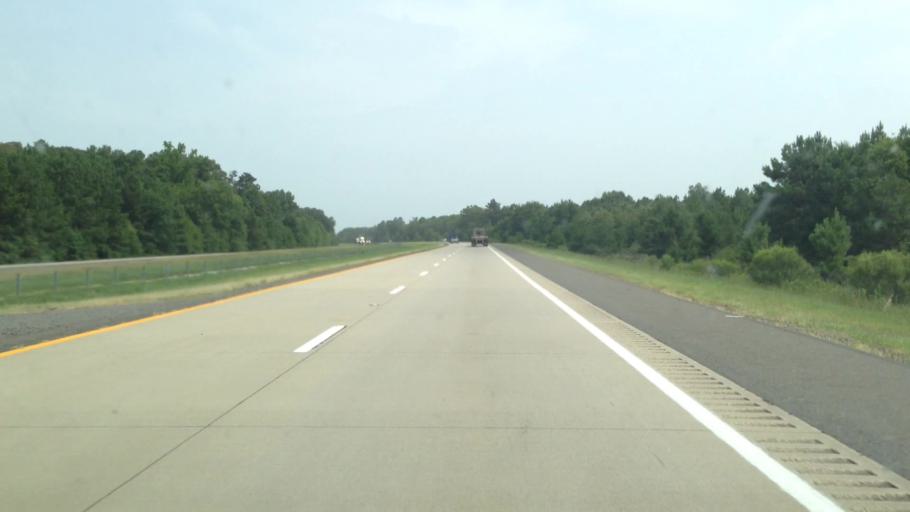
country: US
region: Texas
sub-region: Bowie County
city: Texarkana
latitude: 33.2083
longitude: -93.8750
